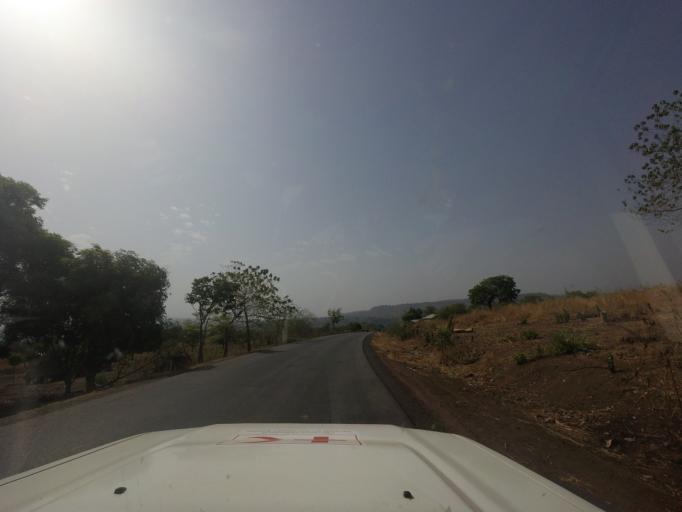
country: GN
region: Mamou
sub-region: Mamou Prefecture
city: Mamou
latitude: 10.1920
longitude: -12.4587
